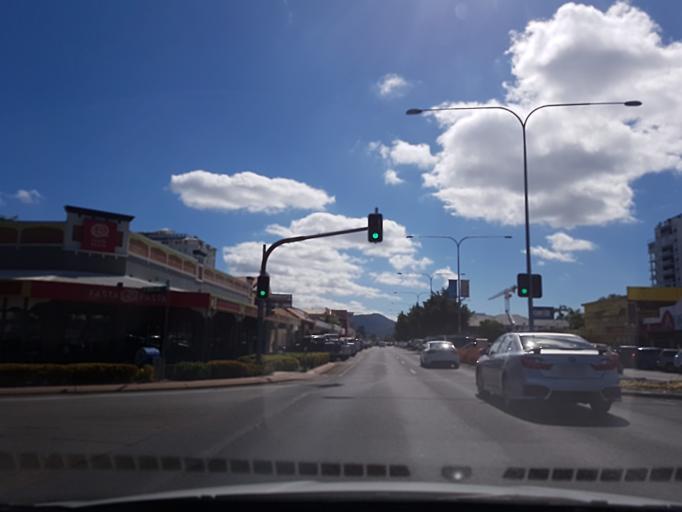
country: AU
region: Queensland
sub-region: Cairns
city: Cairns
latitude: -16.9238
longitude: 145.7737
